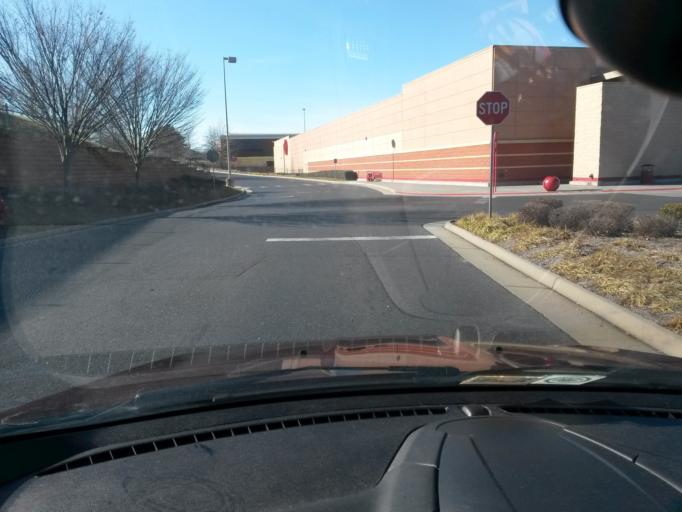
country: US
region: Virginia
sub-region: Rockingham County
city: Massanetta Springs
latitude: 38.4257
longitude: -78.8426
